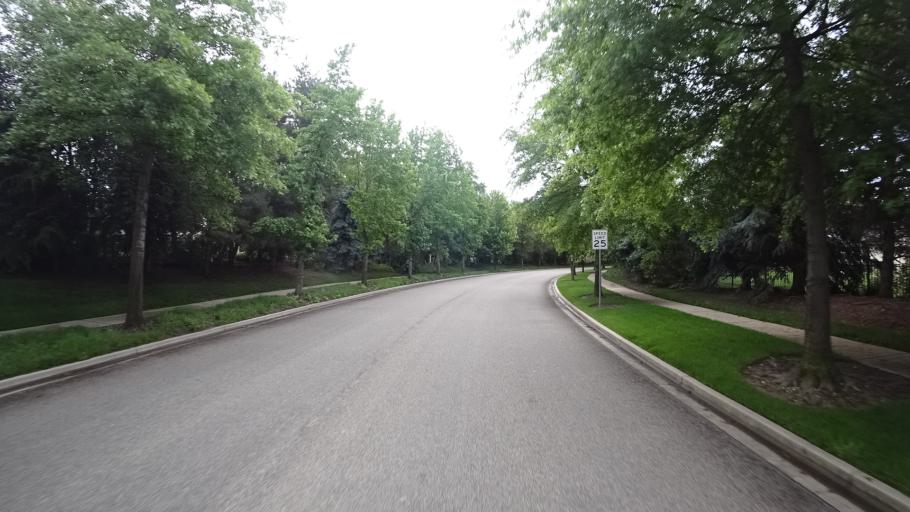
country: US
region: Idaho
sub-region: Ada County
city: Eagle
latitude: 43.6861
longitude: -116.3596
